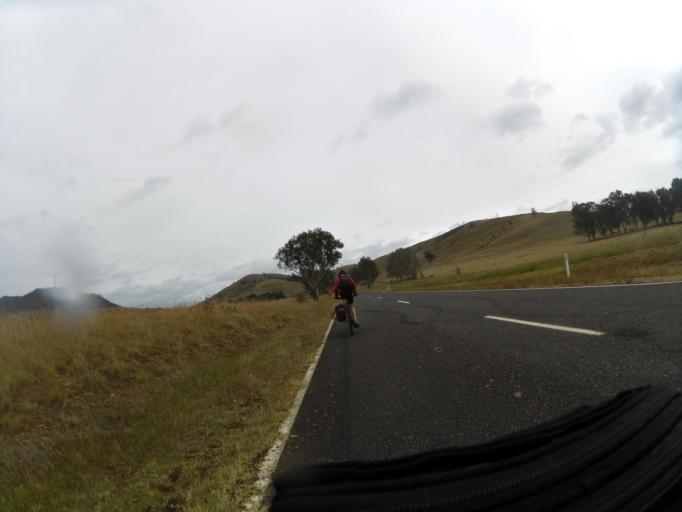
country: AU
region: New South Wales
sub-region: Greater Hume Shire
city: Holbrook
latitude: -36.2065
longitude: 147.7396
